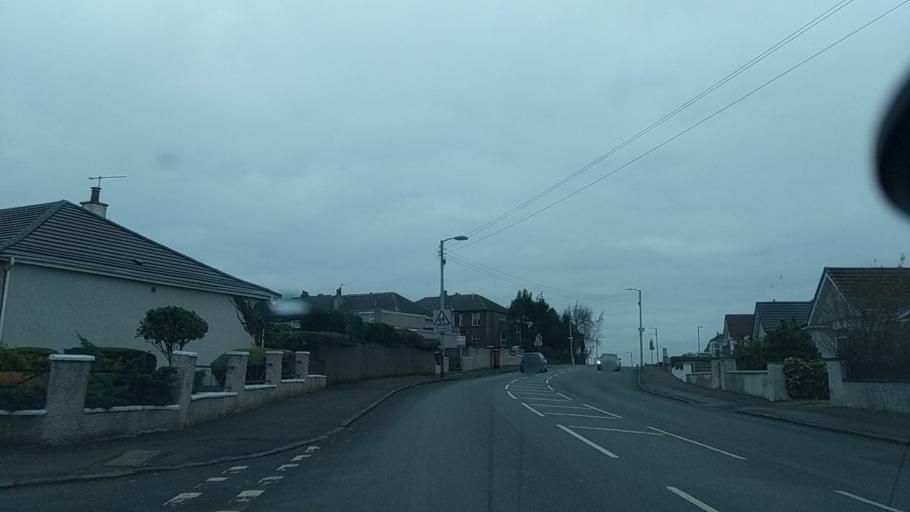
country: GB
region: Scotland
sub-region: South Lanarkshire
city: Rutherglen
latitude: 55.8196
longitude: -4.1931
